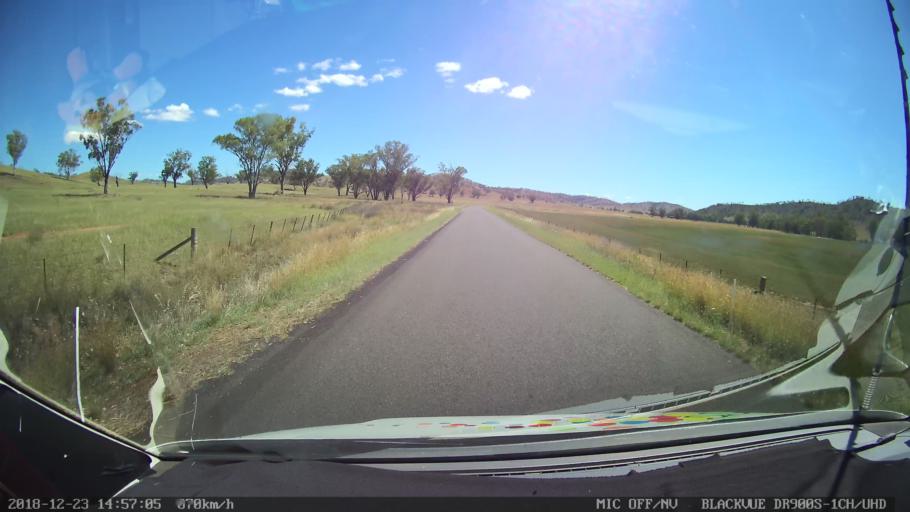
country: AU
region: New South Wales
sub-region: Tamworth Municipality
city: Manilla
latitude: -30.7075
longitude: 150.8277
